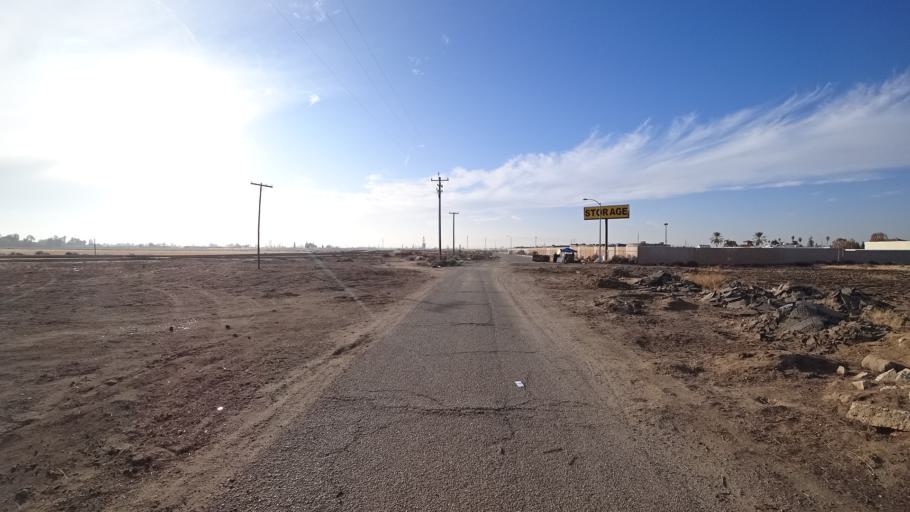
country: US
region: California
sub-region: Kern County
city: Oildale
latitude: 35.4091
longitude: -119.0566
